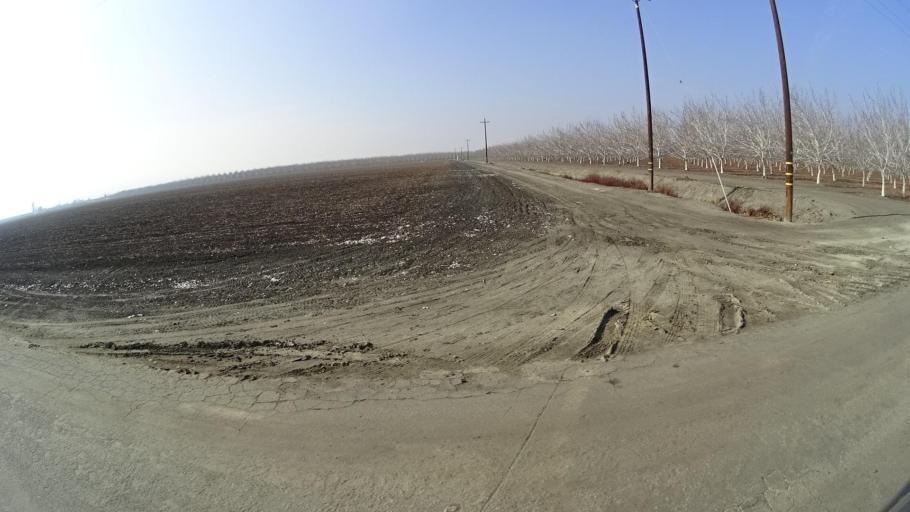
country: US
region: California
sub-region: Kern County
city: Buttonwillow
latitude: 35.3619
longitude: -119.4123
